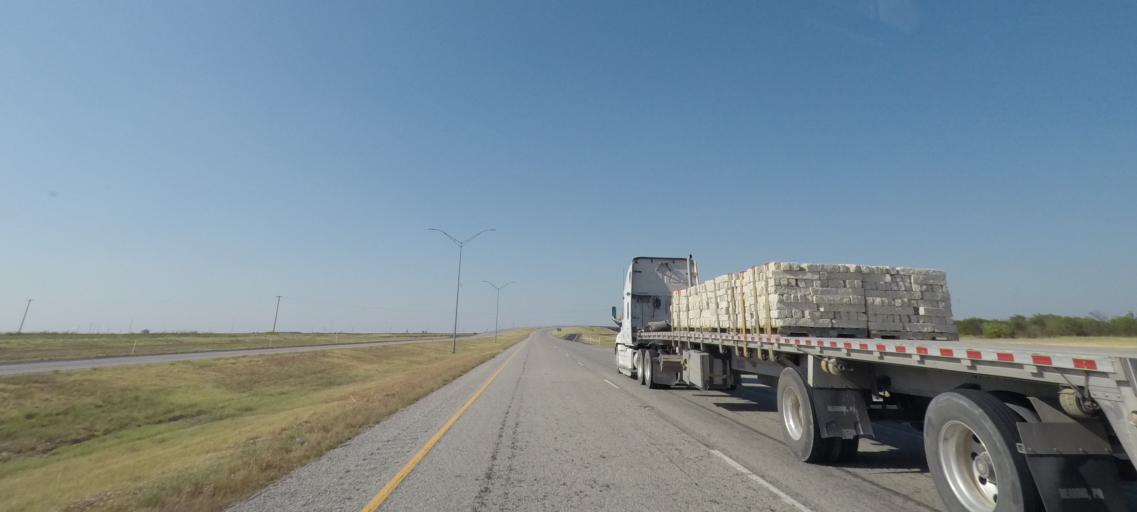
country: US
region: Texas
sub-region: Baylor County
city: Seymour
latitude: 33.6094
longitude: -99.2428
